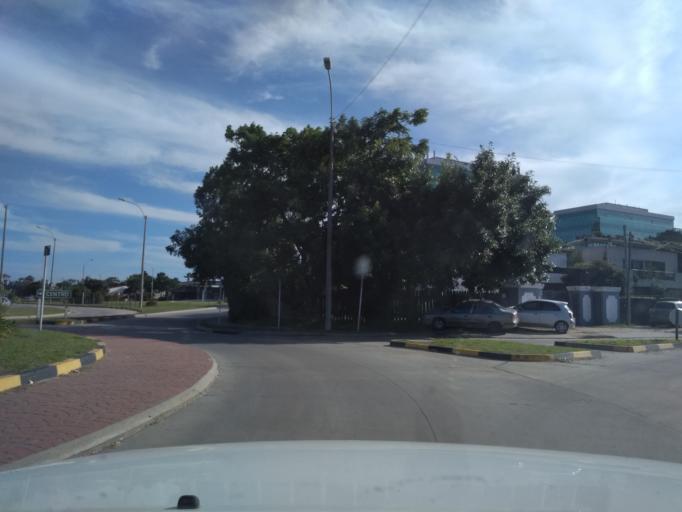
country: UY
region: Canelones
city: Barra de Carrasco
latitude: -34.8743
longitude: -56.0384
